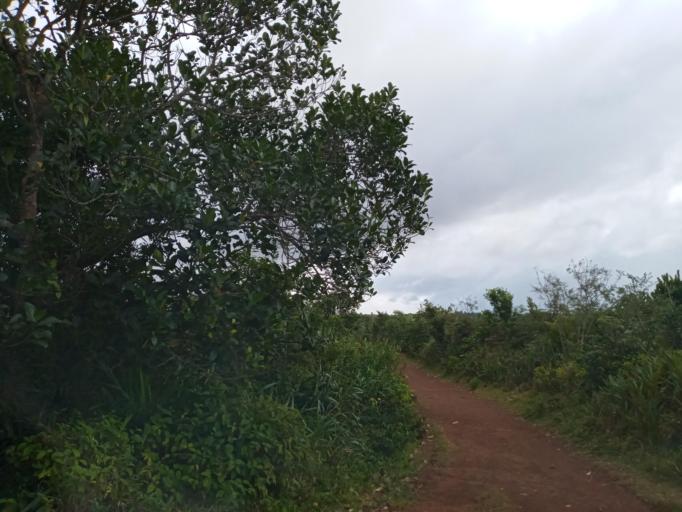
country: MG
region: Atsimo-Atsinanana
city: Vohipaho
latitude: -23.7807
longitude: 47.5422
